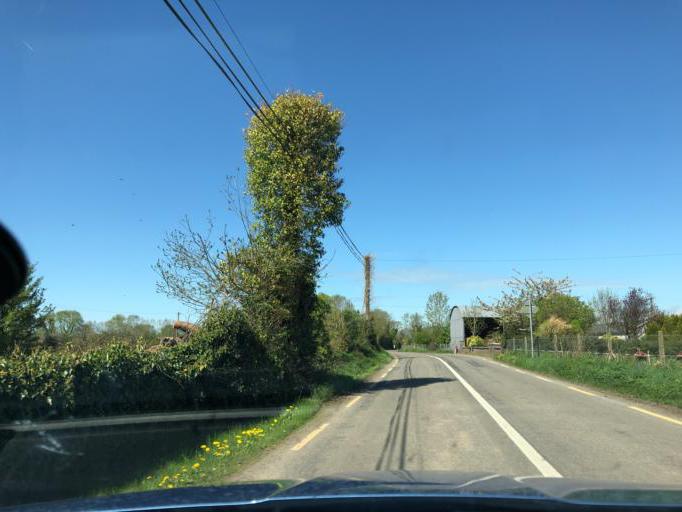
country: IE
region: Connaught
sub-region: County Galway
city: Portumna
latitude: 53.1268
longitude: -8.3433
